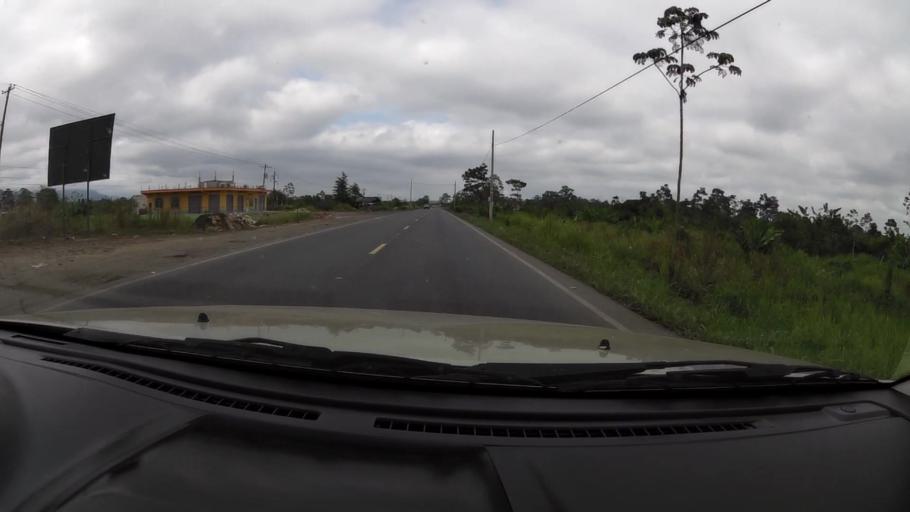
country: EC
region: Guayas
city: Naranjal
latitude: -2.6861
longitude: -79.6317
